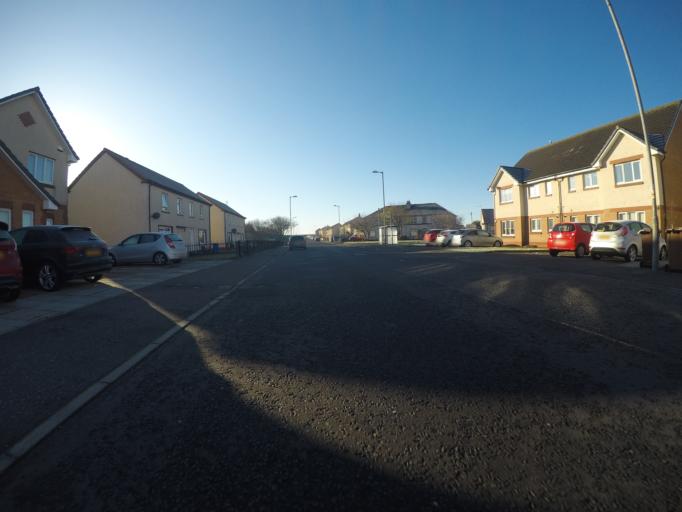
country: GB
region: Scotland
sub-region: North Ayrshire
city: Stevenston
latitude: 55.6328
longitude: -4.7429
